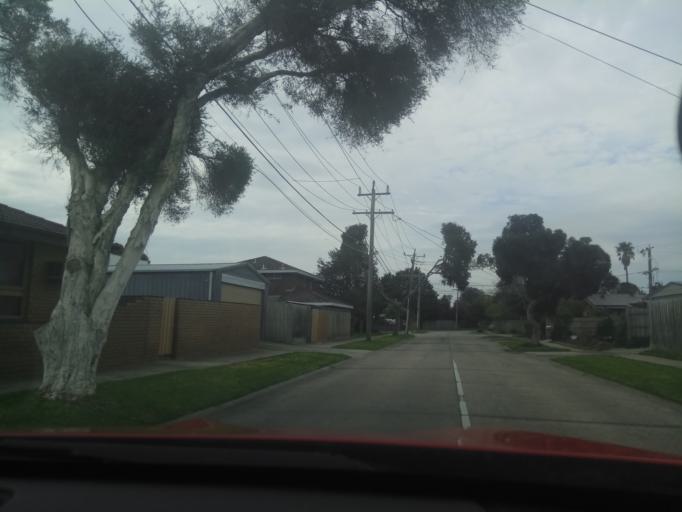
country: AU
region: Victoria
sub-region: Kingston
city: Aspendale
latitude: -38.0231
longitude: 145.1062
